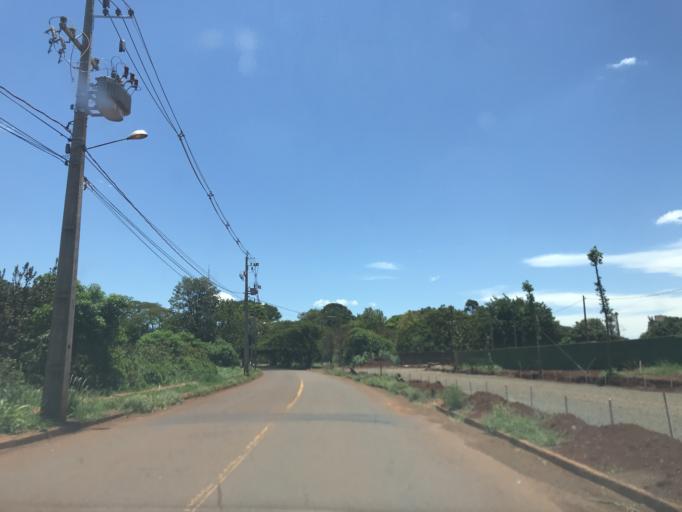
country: BR
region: Parana
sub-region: Sarandi
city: Sarandi
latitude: -23.4420
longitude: -51.9052
